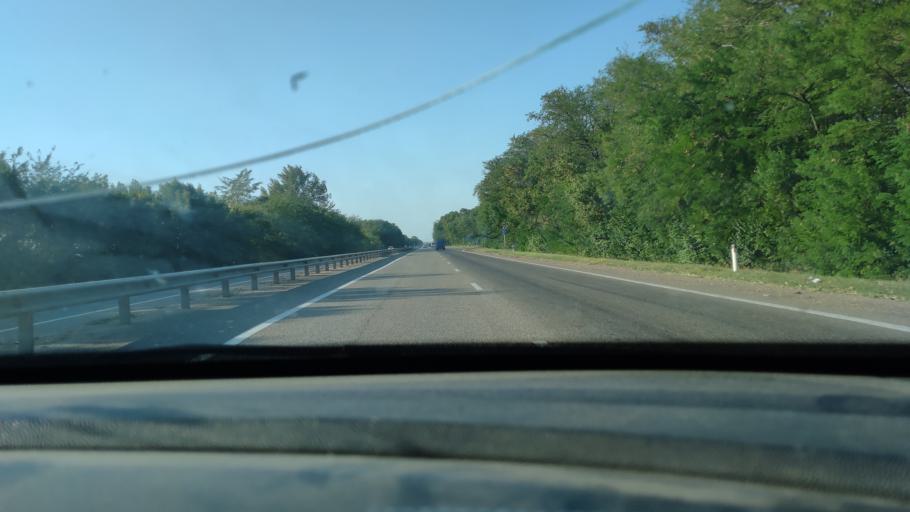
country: RU
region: Krasnodarskiy
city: Timashevsk
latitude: 45.5350
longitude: 38.9382
